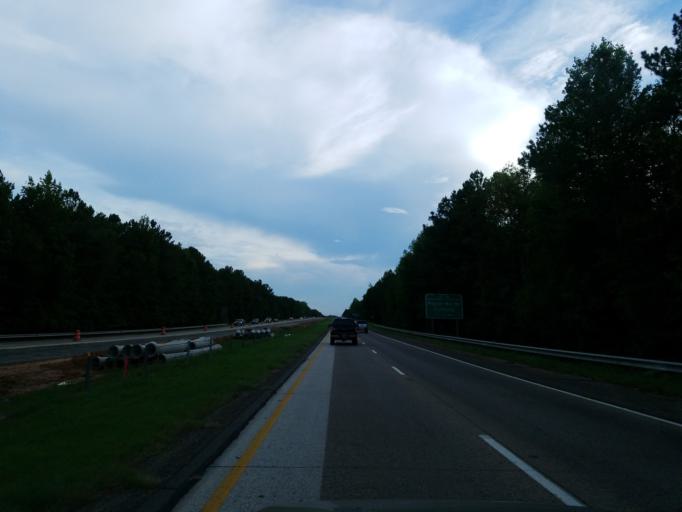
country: US
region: Georgia
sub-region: Forsyth County
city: Cumming
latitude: 34.2404
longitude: -84.0976
